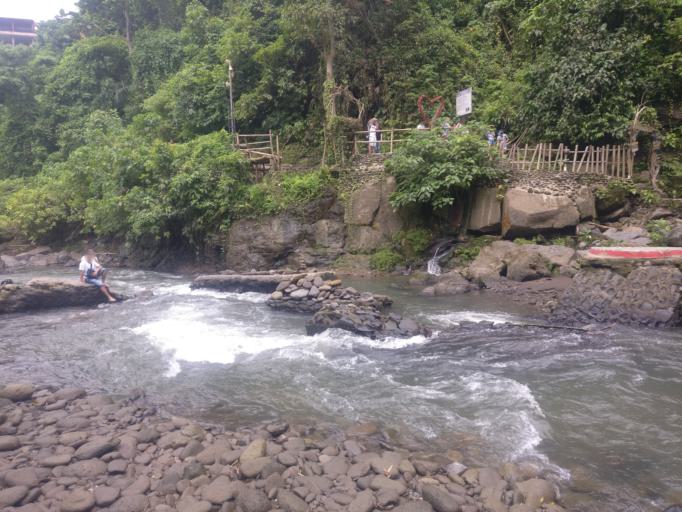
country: ID
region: Bali
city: Banjar Desa
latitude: -8.5753
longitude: 115.2903
